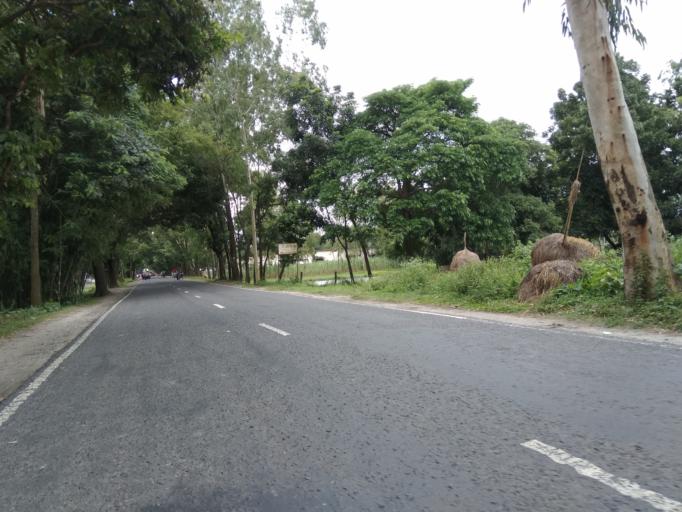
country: BD
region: Rajshahi
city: Saidpur
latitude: 25.7724
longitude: 88.7975
